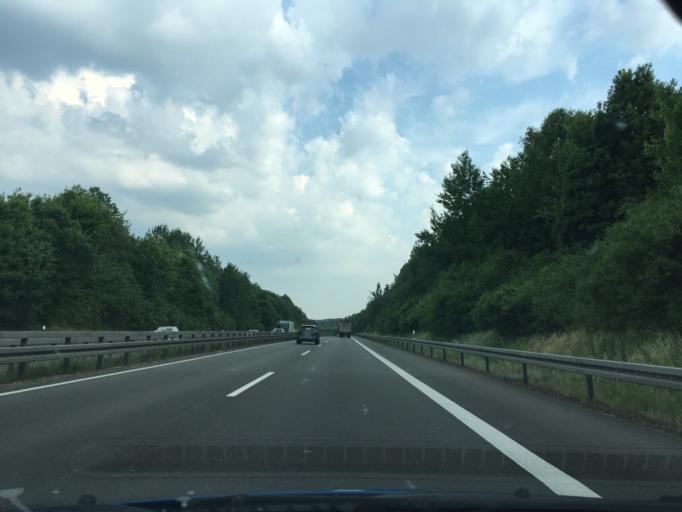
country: DE
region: Lower Saxony
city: Stelle
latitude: 53.3655
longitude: 10.1082
